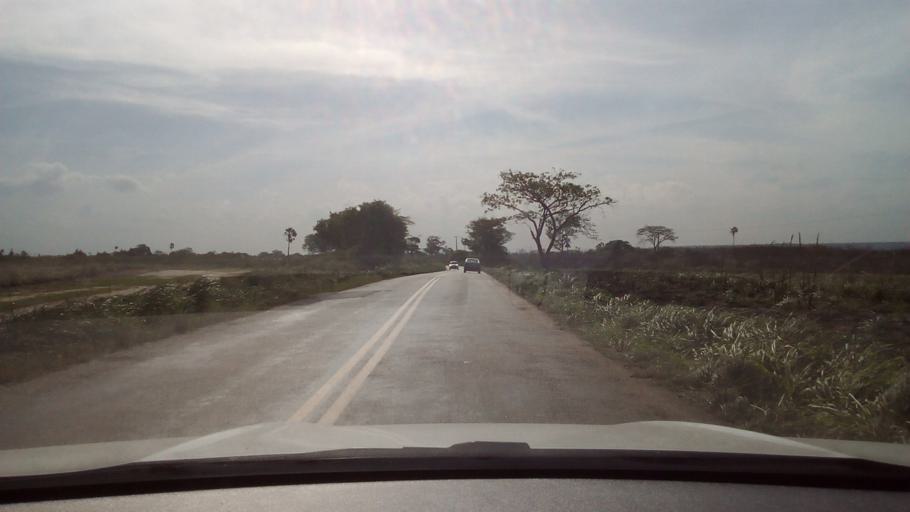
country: BR
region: Rio Grande do Norte
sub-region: Goianinha
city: Goianinha
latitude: -6.2536
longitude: -35.1901
